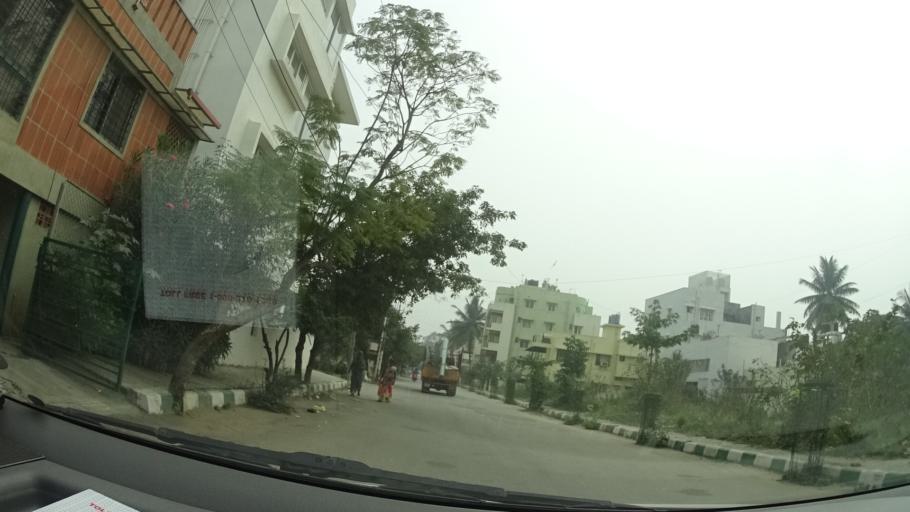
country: IN
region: Karnataka
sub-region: Bangalore Urban
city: Yelahanka
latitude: 13.0401
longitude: 77.6269
